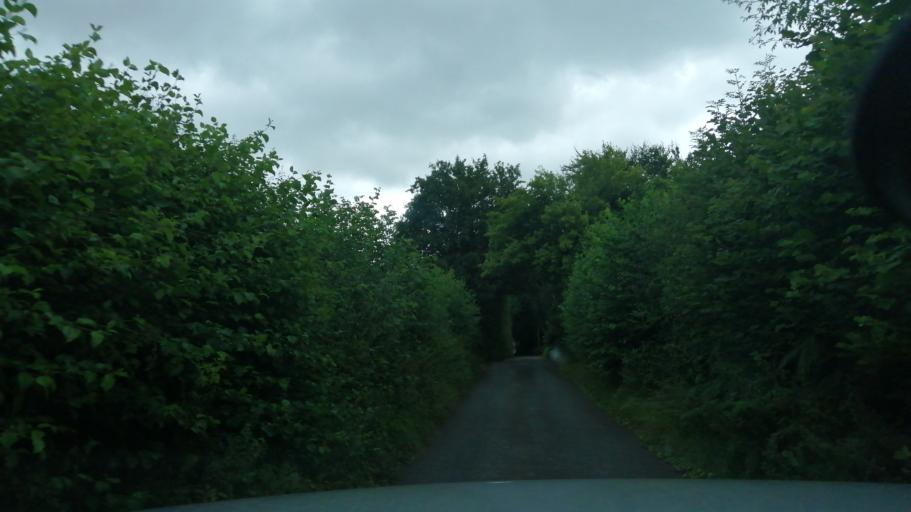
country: GB
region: England
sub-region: Herefordshire
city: Madley
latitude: 52.0235
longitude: -2.8617
